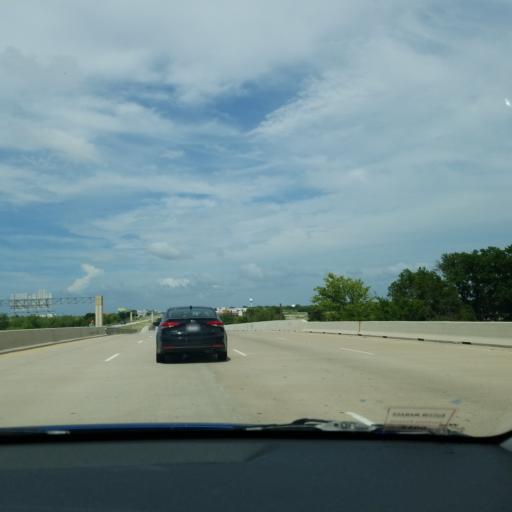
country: US
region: Texas
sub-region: Travis County
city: Manor
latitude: 30.3462
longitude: -97.5708
